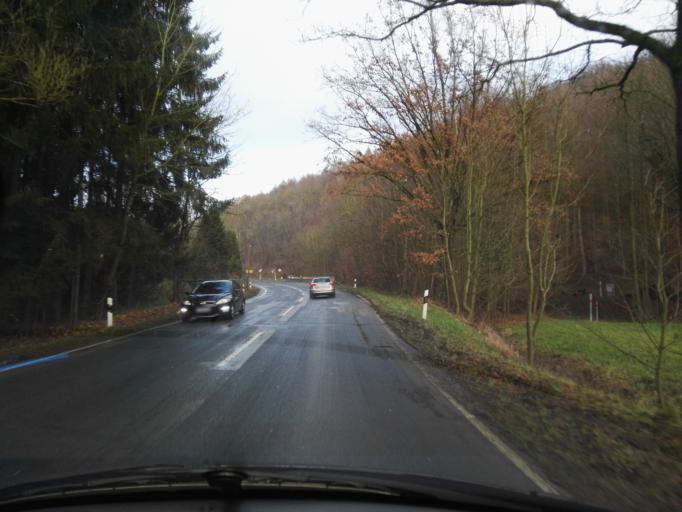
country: DE
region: Lower Saxony
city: Diekholzen
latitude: 52.0896
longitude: 9.9153
